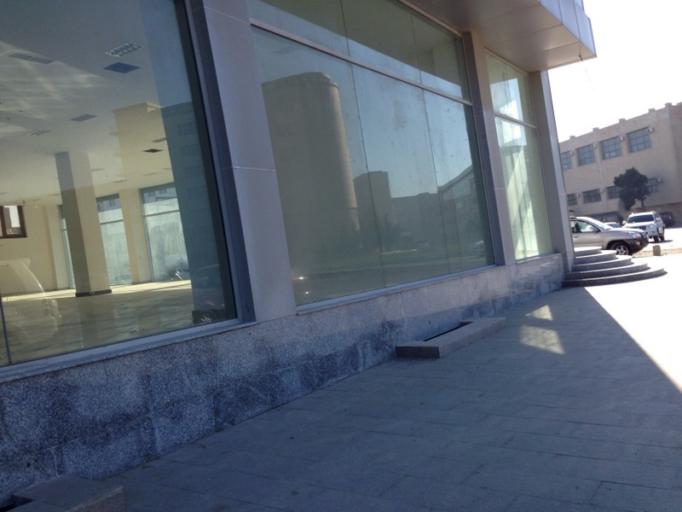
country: AZ
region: Baki
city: Baku
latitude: 40.4055
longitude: 49.8620
